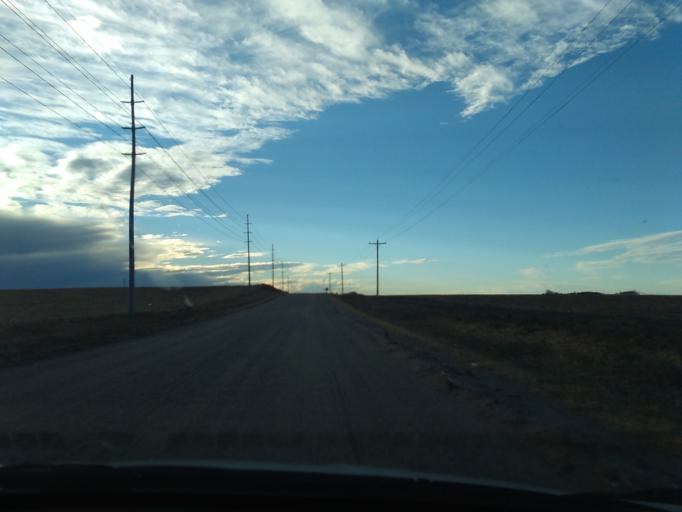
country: US
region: Nebraska
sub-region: Phelps County
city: Holdrege
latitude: 40.4088
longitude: -99.3655
